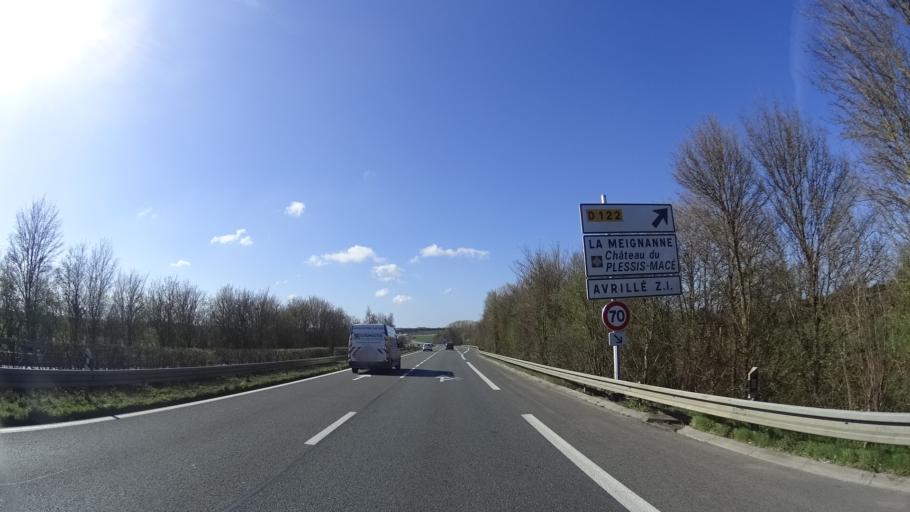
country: FR
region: Pays de la Loire
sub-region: Departement de Maine-et-Loire
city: Beaucouze
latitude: 47.5033
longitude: -0.6192
